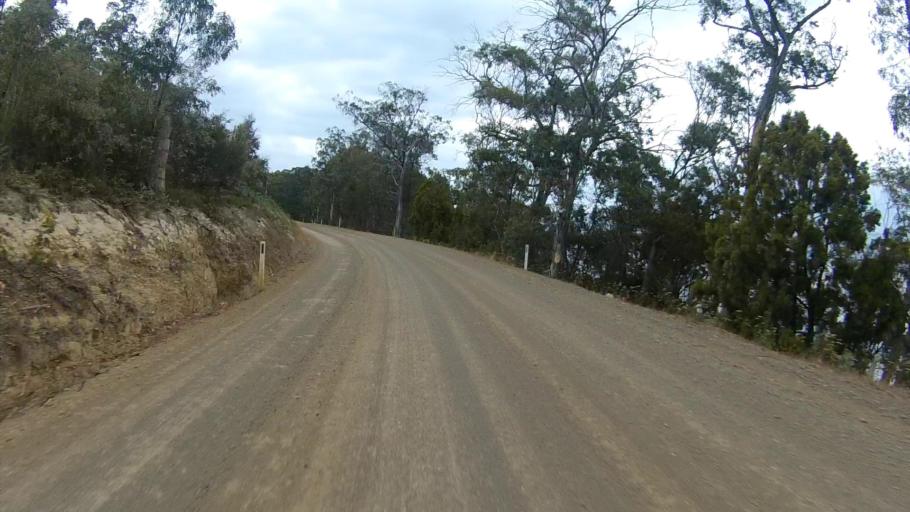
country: AU
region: Tasmania
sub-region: Huon Valley
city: Cygnet
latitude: -43.2210
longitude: 147.0921
